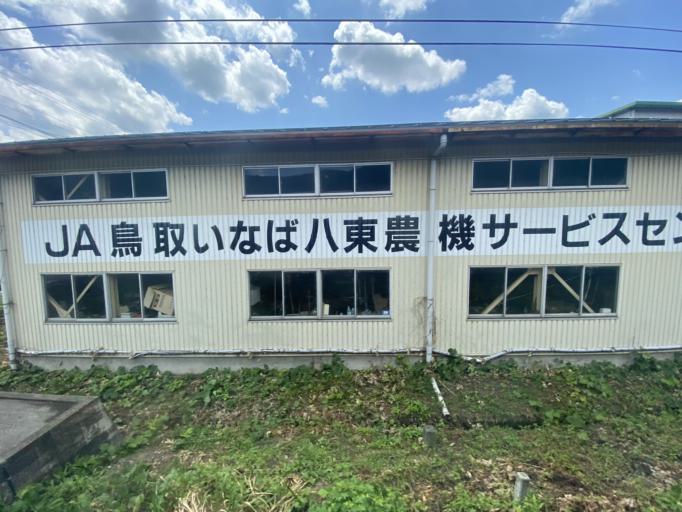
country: JP
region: Tottori
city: Tottori
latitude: 35.3645
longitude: 134.3350
